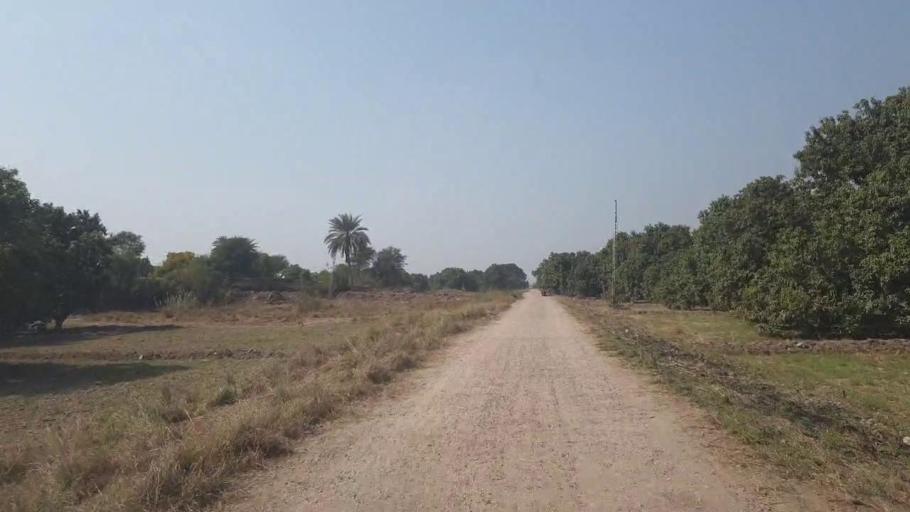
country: PK
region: Sindh
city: Tando Allahyar
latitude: 25.4591
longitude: 68.8025
